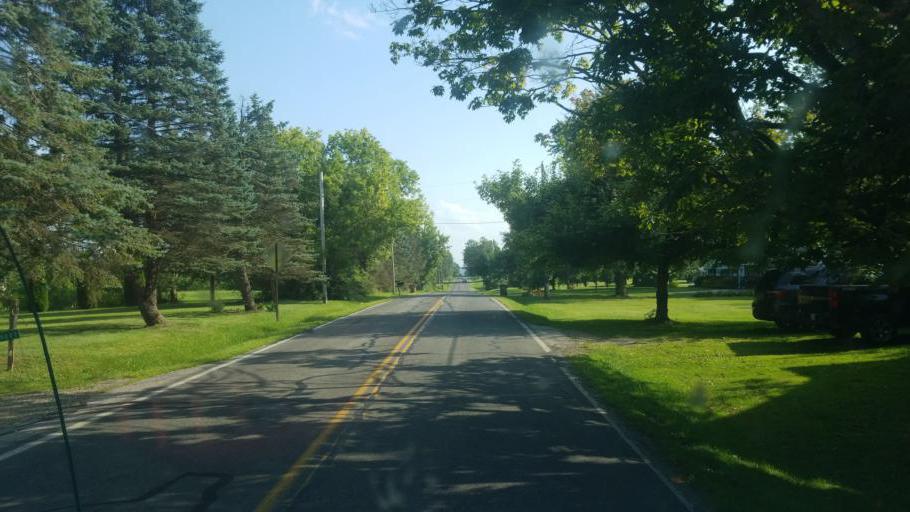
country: US
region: Ohio
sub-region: Medina County
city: Westfield Center
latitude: 41.0254
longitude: -81.9665
